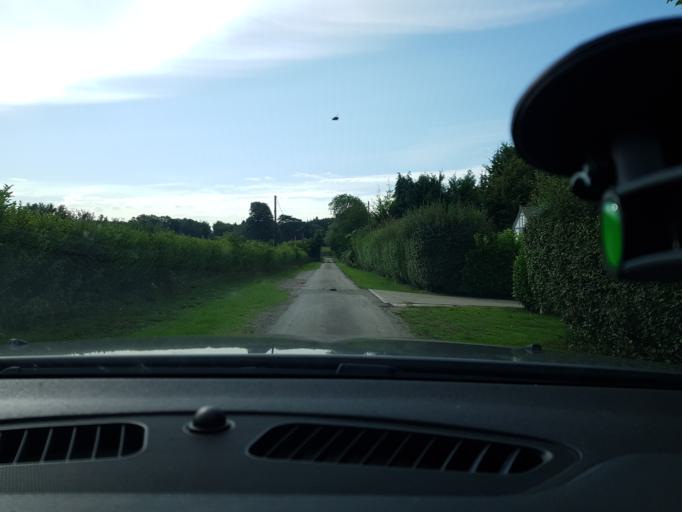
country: GB
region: England
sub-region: West Berkshire
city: Kintbury
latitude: 51.3985
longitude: -1.4833
